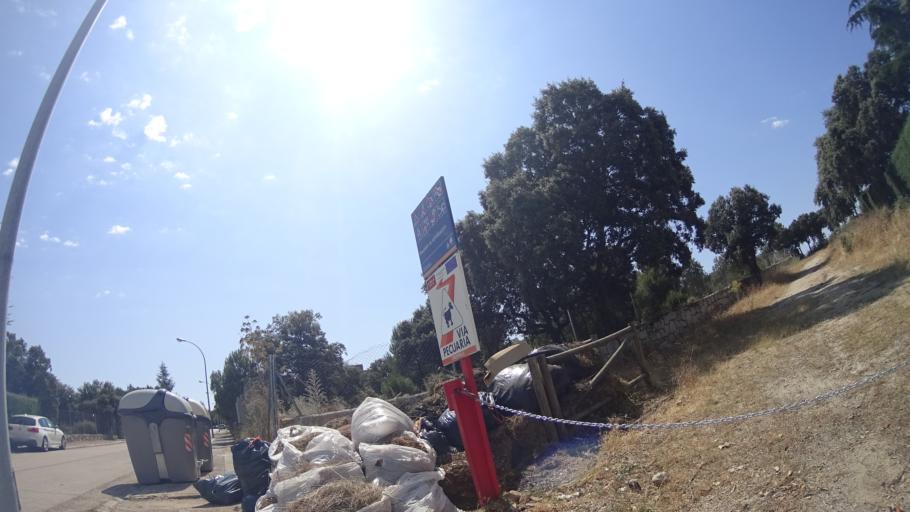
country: ES
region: Madrid
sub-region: Provincia de Madrid
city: Torrelodones
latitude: 40.5999
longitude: -3.9414
